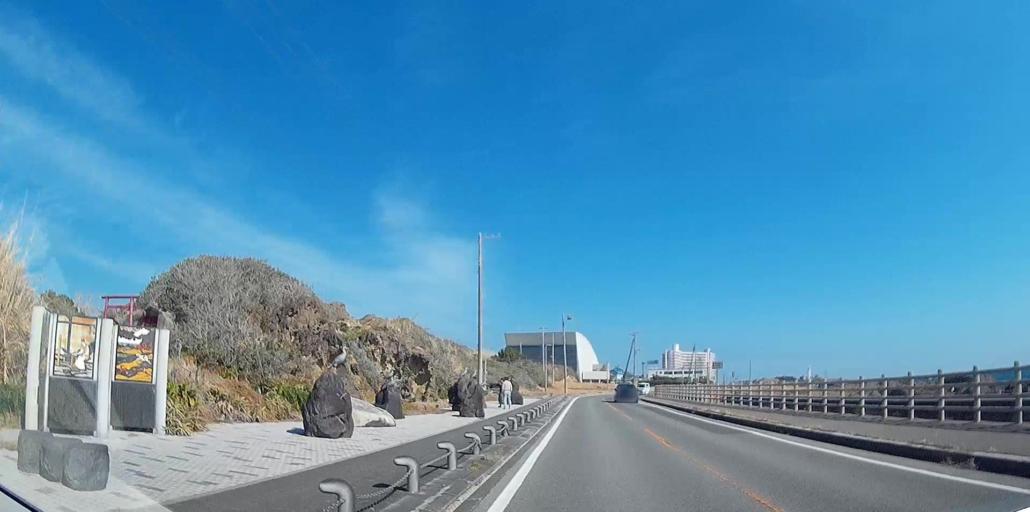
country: JP
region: Chiba
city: Tateyama
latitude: 34.9042
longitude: 139.8756
